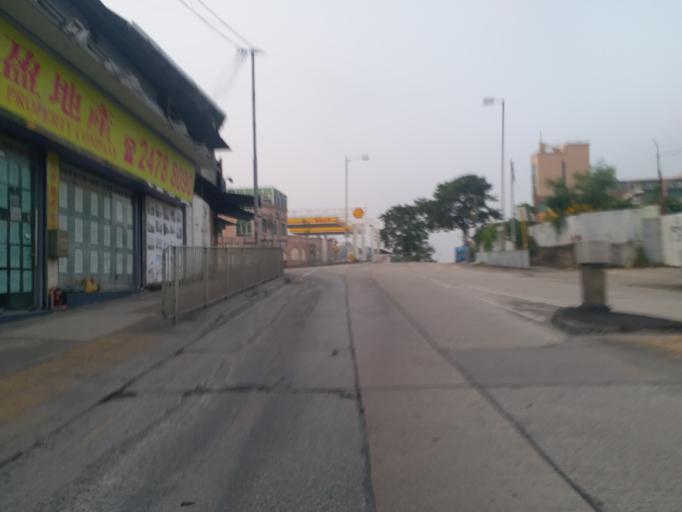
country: HK
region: Yuen Long
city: Yuen Long Kau Hui
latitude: 22.4390
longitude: 114.0111
